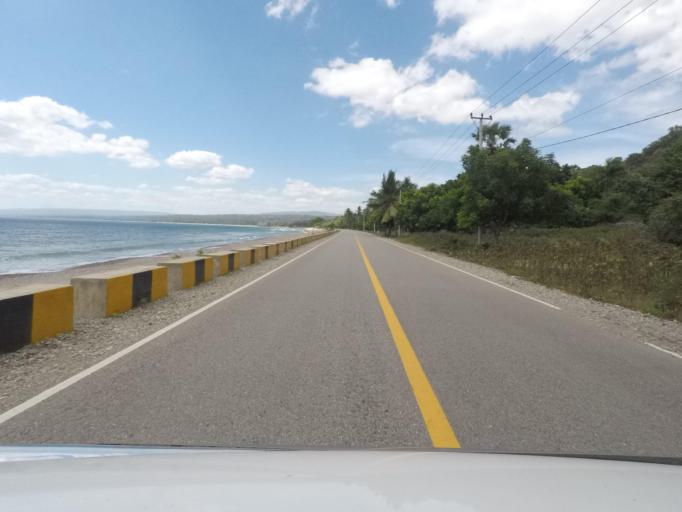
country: TL
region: Lautem
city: Lospalos
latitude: -8.4175
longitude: 126.7506
